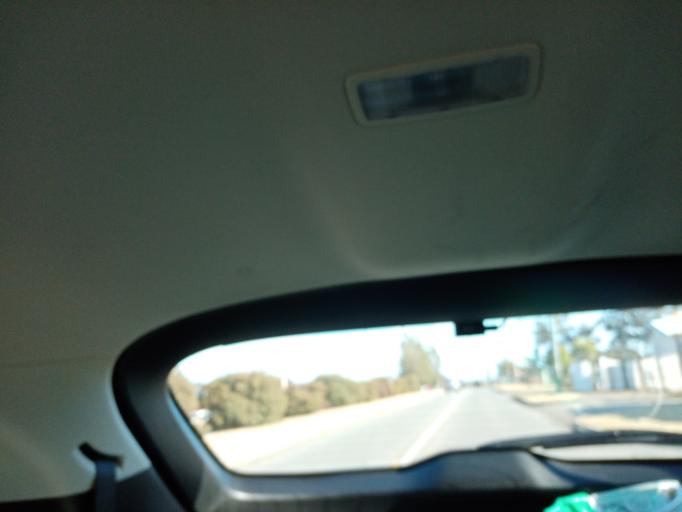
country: AU
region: Western Australia
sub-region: City of Cockburn
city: South Lake
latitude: -32.1213
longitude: 115.8403
